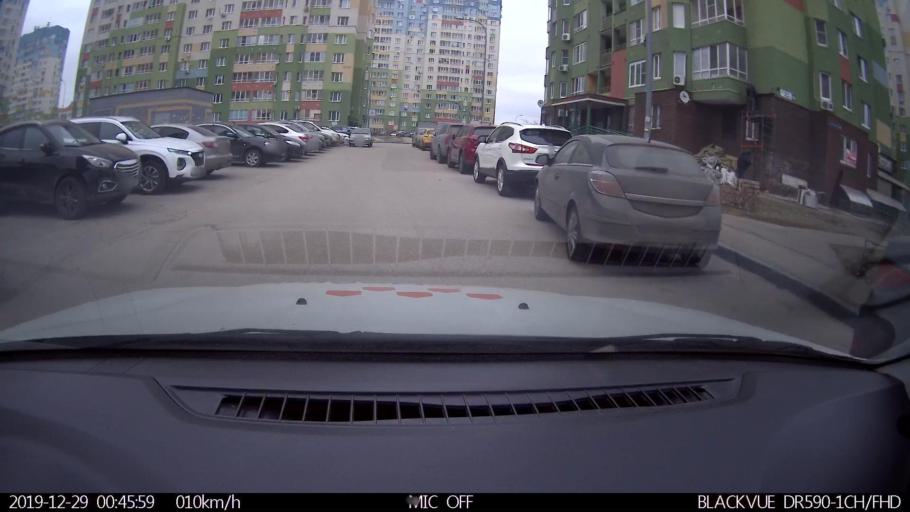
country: RU
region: Nizjnij Novgorod
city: Nizhniy Novgorod
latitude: 56.3405
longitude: 43.9507
